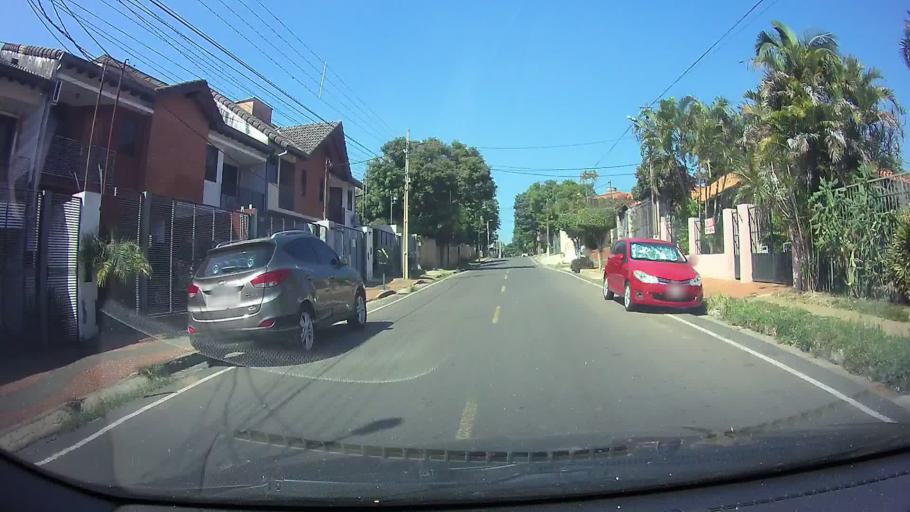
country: PY
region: Central
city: Fernando de la Mora
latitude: -25.2640
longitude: -57.5128
